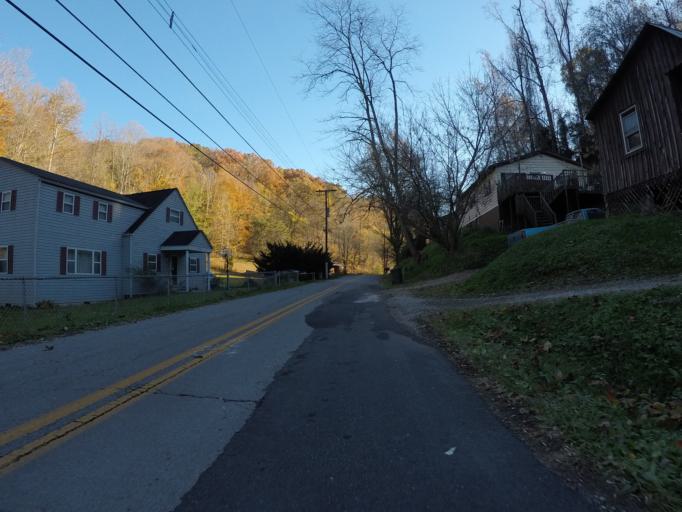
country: US
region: West Virginia
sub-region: Wayne County
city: Kenova
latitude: 38.3887
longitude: -82.5712
